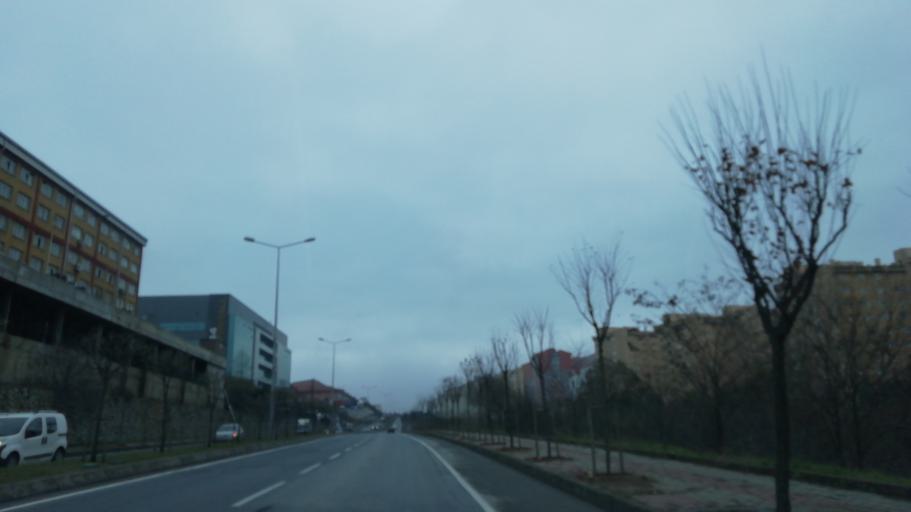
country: TR
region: Istanbul
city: Basaksehir
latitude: 41.0925
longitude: 28.8024
